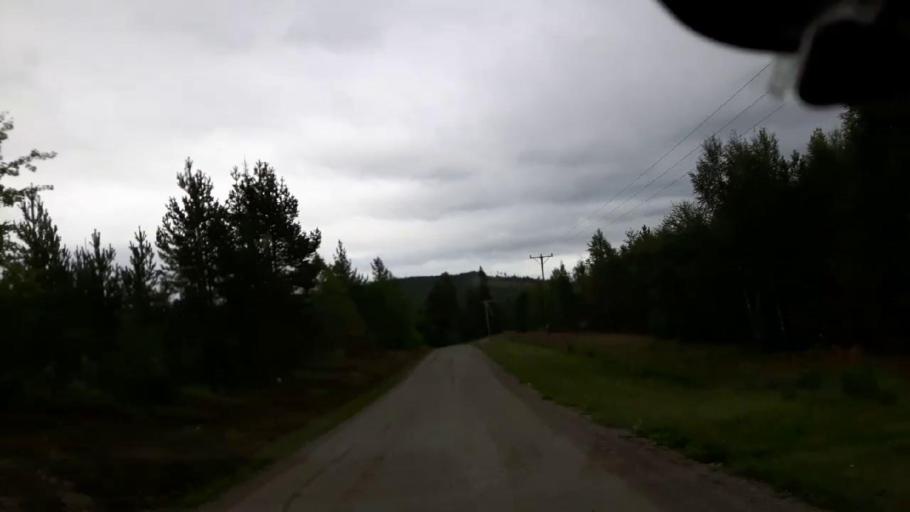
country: SE
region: Vaesternorrland
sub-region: Ange Kommun
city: Fransta
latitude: 62.7786
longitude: 16.2173
